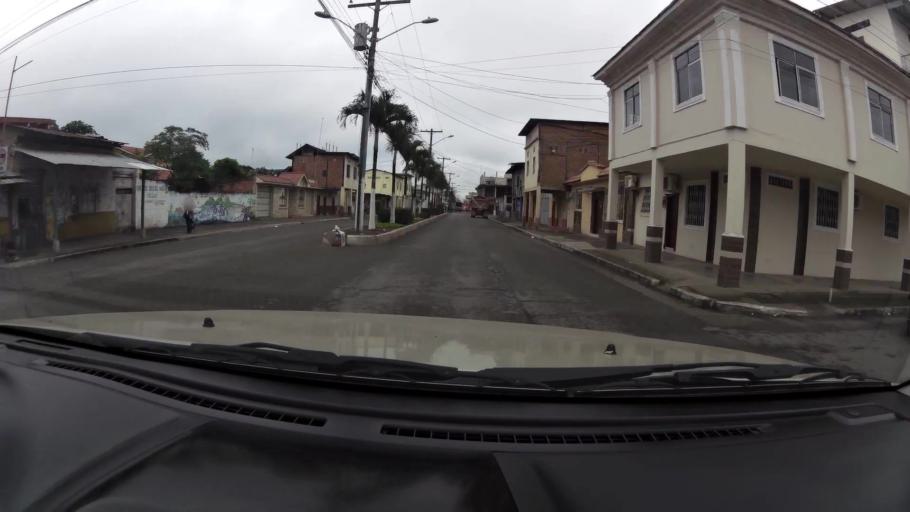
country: EC
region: El Oro
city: Pasaje
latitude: -3.3244
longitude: -79.8029
